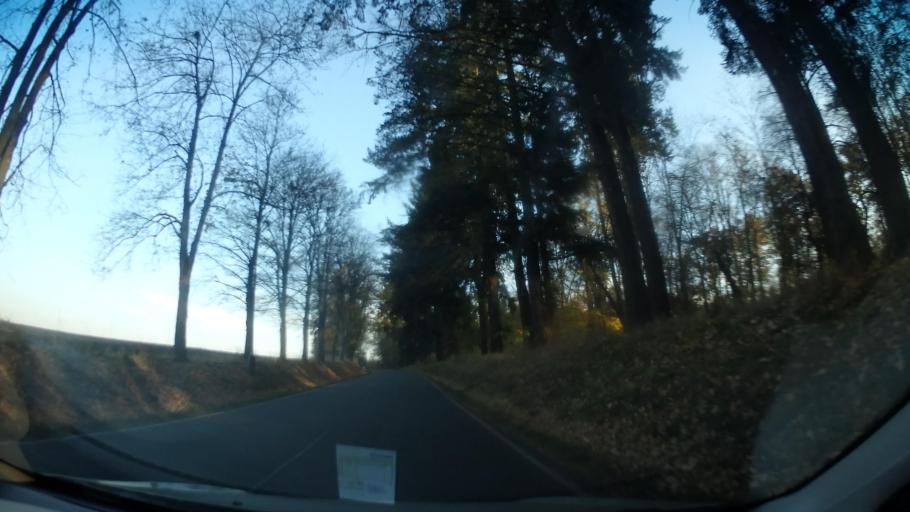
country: CZ
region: Central Bohemia
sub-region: Okres Benesov
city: Benesov
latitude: 49.7812
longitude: 14.6672
